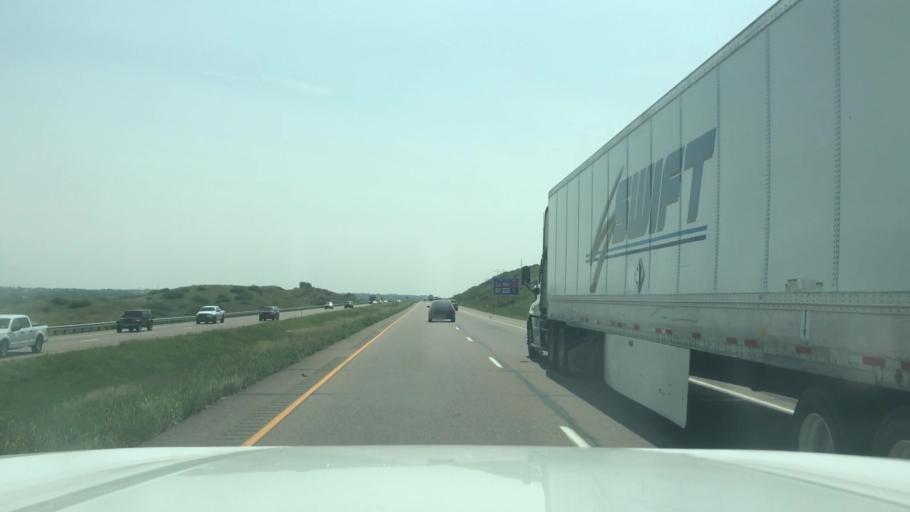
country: US
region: Colorado
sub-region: El Paso County
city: Security-Widefield
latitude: 38.7371
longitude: -104.7455
